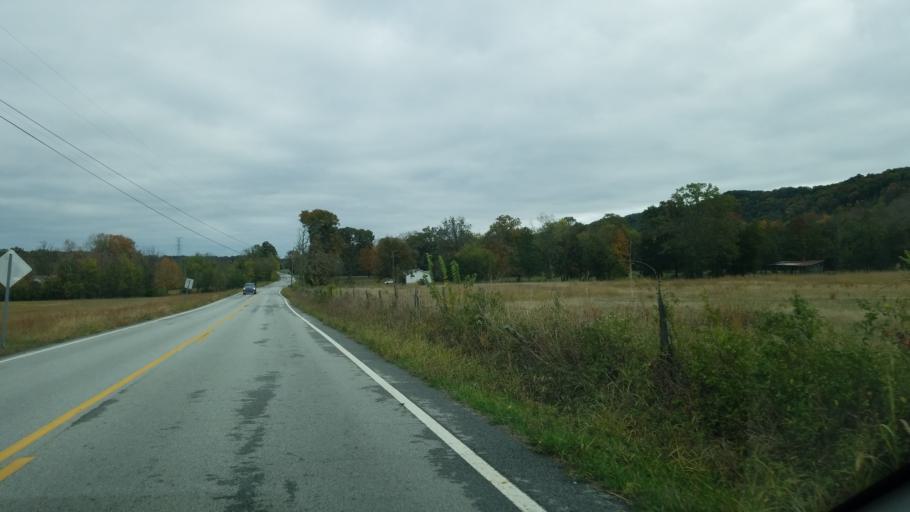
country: US
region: Tennessee
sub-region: Hamilton County
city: Lakesite
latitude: 35.2063
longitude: -85.0102
